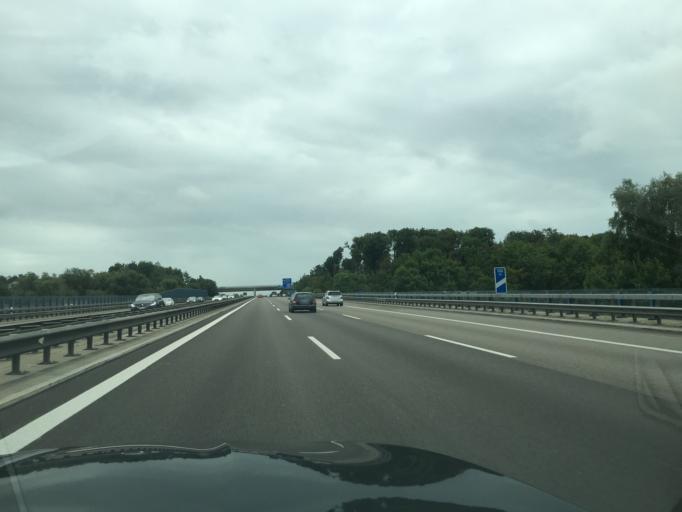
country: DE
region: Bavaria
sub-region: Swabia
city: Leipheim
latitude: 48.4478
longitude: 10.2055
